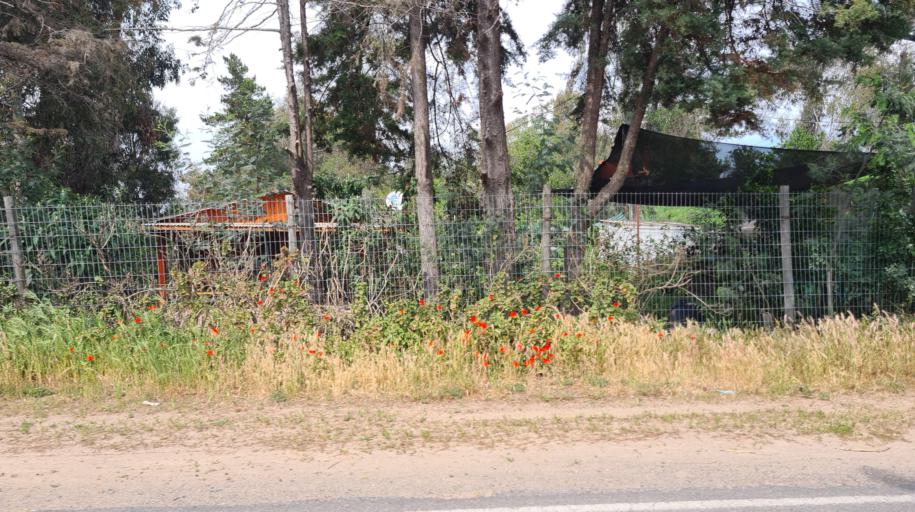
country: CL
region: O'Higgins
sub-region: Provincia de Cachapoal
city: San Vicente
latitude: -34.1506
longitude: -71.4569
